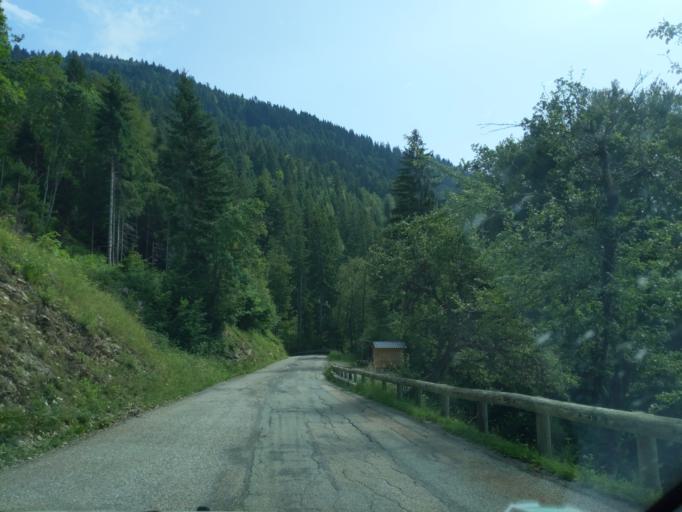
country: FR
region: Rhone-Alpes
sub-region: Departement de la Savoie
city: Ugine
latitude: 45.7474
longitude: 6.4705
